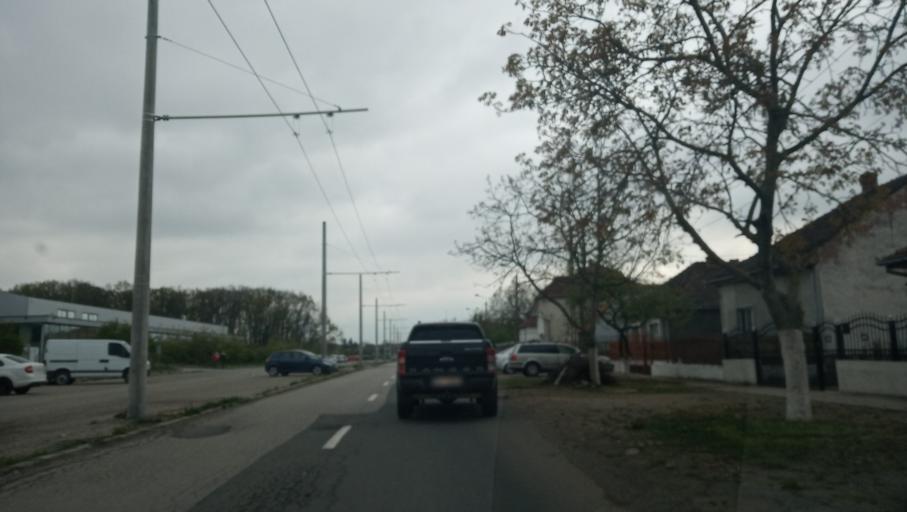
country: RO
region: Timis
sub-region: Comuna Ghiroda
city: Ghiroda
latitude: 45.7675
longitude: 21.2685
